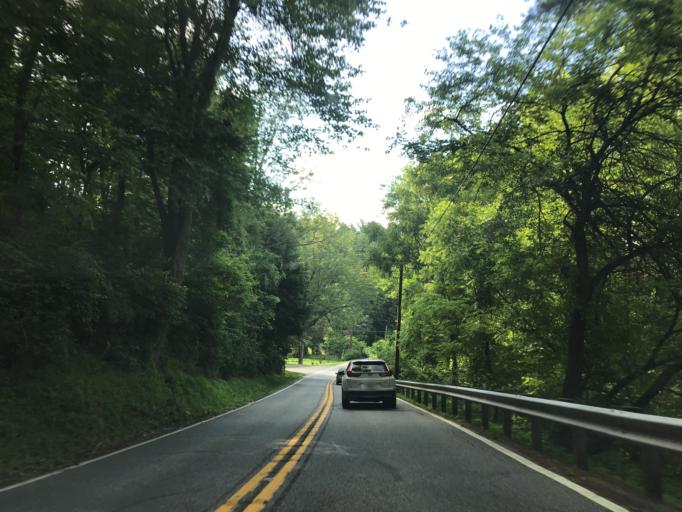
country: US
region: Maryland
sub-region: Carroll County
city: Hampstead
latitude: 39.5789
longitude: -76.7575
